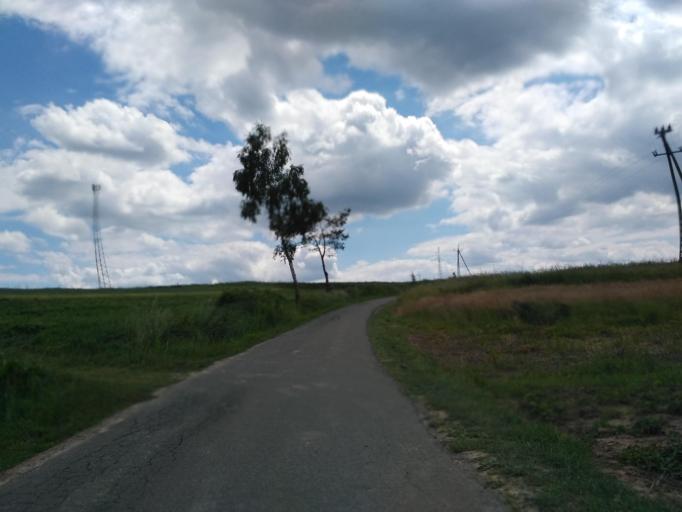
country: PL
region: Subcarpathian Voivodeship
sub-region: Powiat brzozowski
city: Nozdrzec
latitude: 49.7668
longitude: 22.1963
